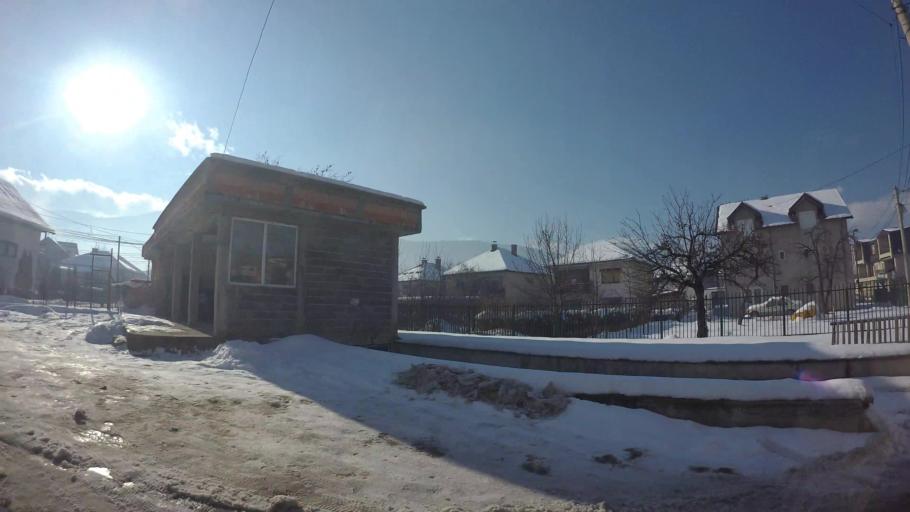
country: BA
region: Federation of Bosnia and Herzegovina
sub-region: Kanton Sarajevo
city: Sarajevo
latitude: 43.8133
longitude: 18.3178
